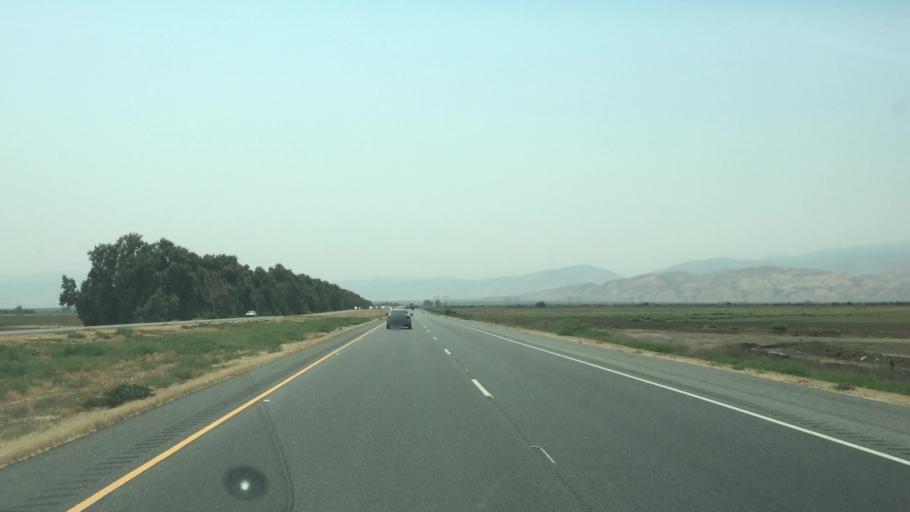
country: US
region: California
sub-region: Kern County
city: Greenfield
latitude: 35.1207
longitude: -119.0658
